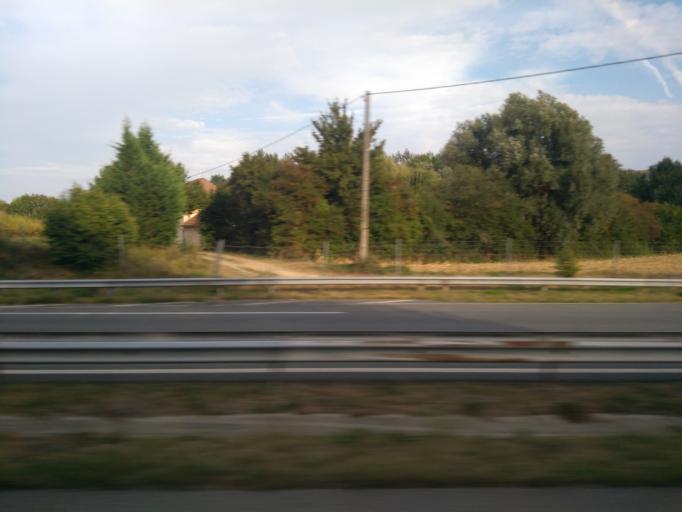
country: FR
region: Rhone-Alpes
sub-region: Departement de l'Isere
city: Saint-Victor-de-Cessieu
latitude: 45.5041
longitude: 5.4001
